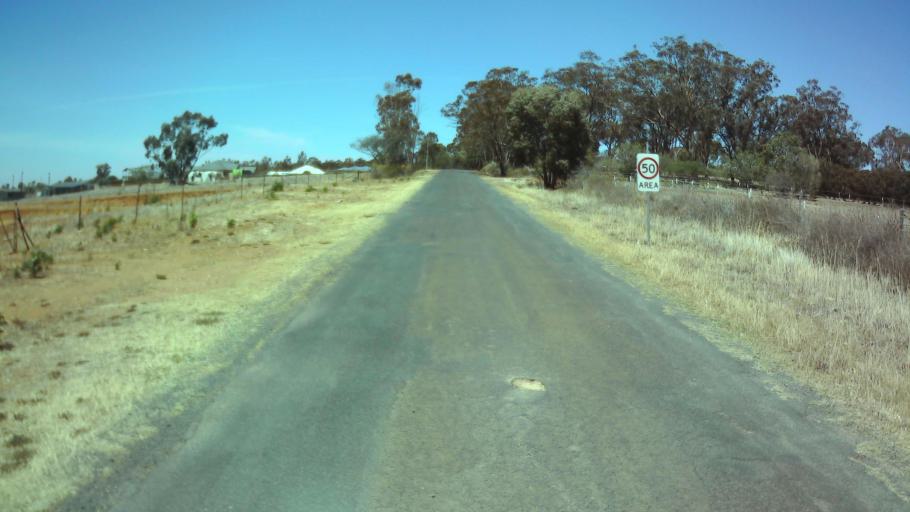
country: AU
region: New South Wales
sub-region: Weddin
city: Grenfell
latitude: -33.9013
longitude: 148.1735
